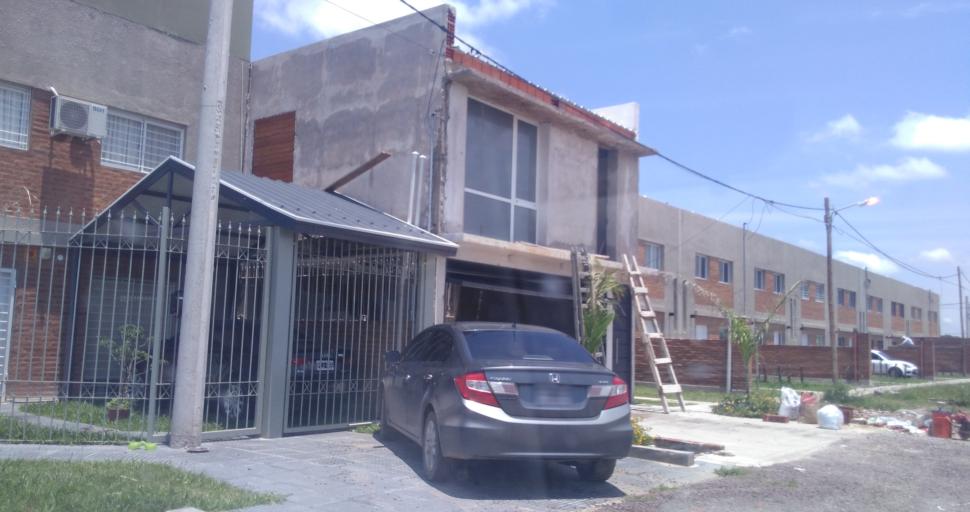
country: AR
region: Chaco
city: Fontana
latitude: -27.4070
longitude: -58.9851
